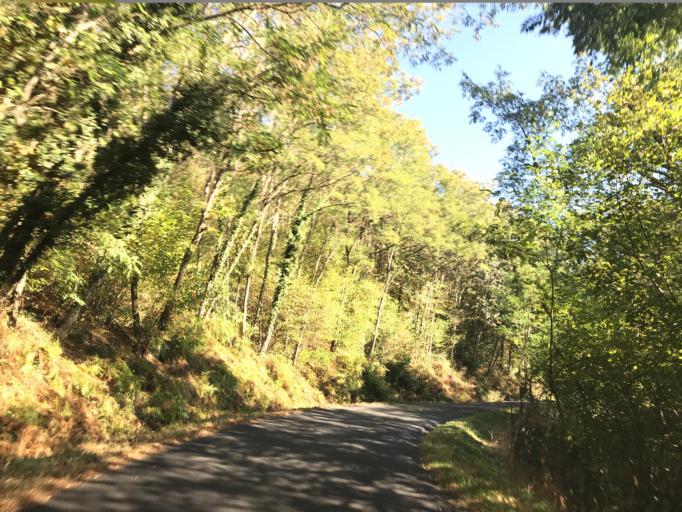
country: FR
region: Auvergne
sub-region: Departement du Puy-de-Dome
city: Escoutoux
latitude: 45.7884
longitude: 3.6156
